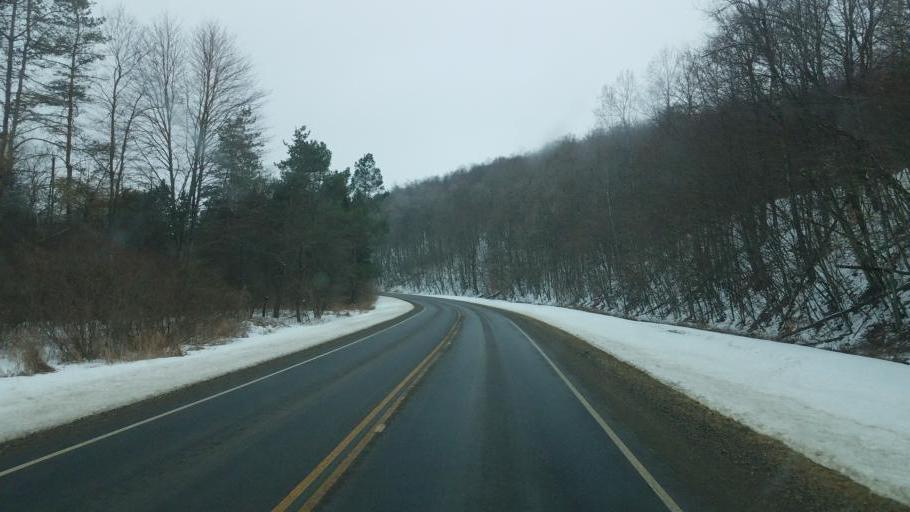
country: US
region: New York
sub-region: Allegany County
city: Andover
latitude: 42.0265
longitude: -77.7504
